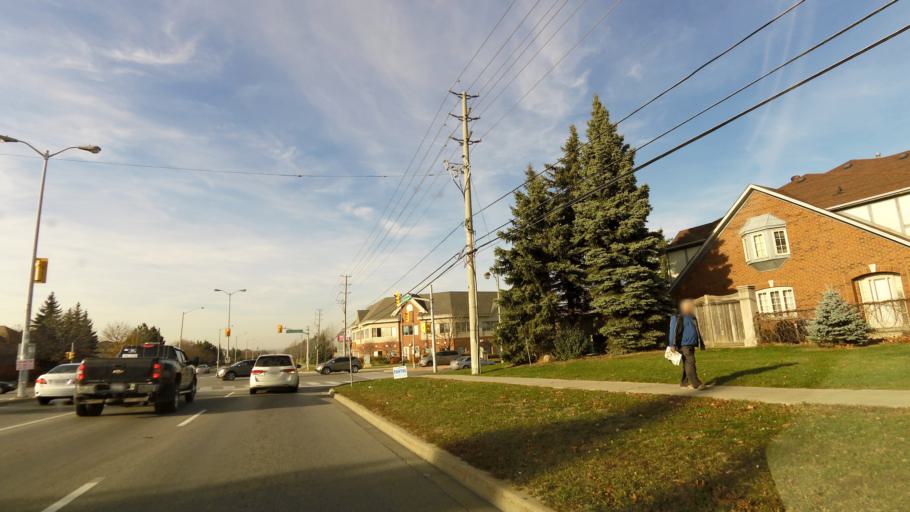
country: CA
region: Ontario
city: Brampton
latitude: 43.7565
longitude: -79.7366
